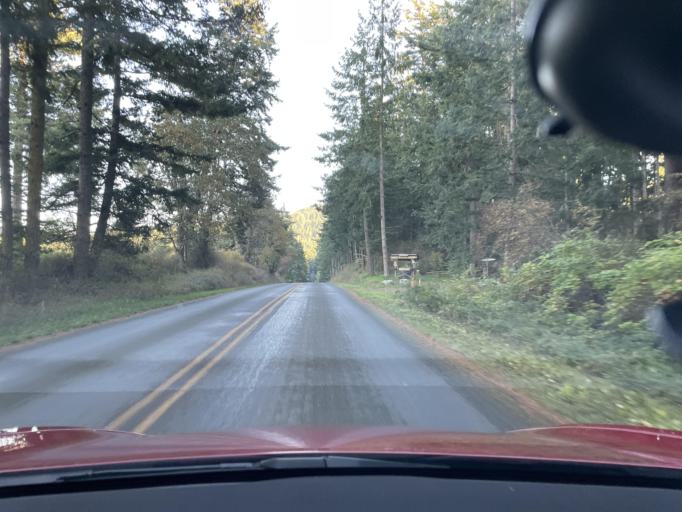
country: US
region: Washington
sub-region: San Juan County
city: Friday Harbor
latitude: 48.5615
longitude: -123.1508
